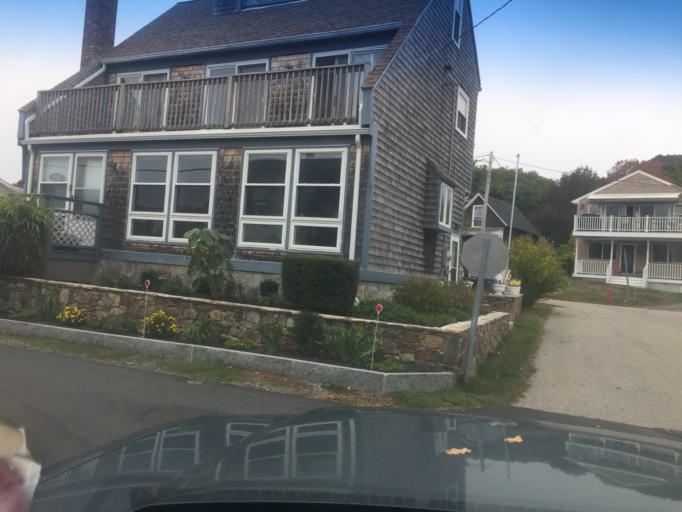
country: US
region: Maine
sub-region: York County
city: York Beach
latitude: 43.1771
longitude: -70.6088
